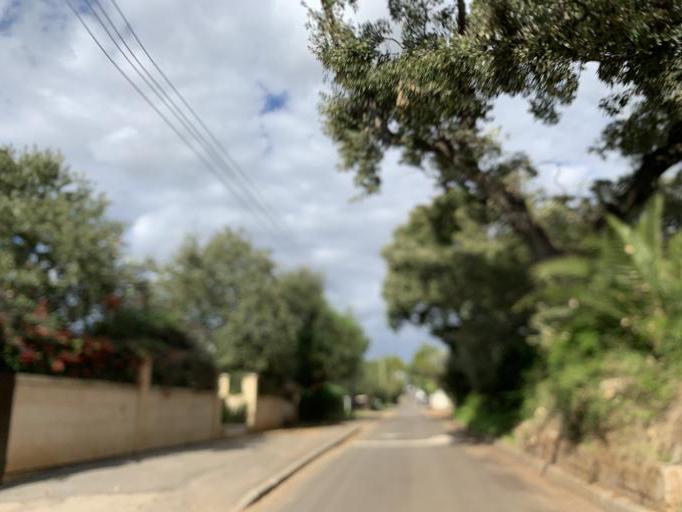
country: IL
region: Central District
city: Hod HaSharon
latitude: 32.1679
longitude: 34.8897
